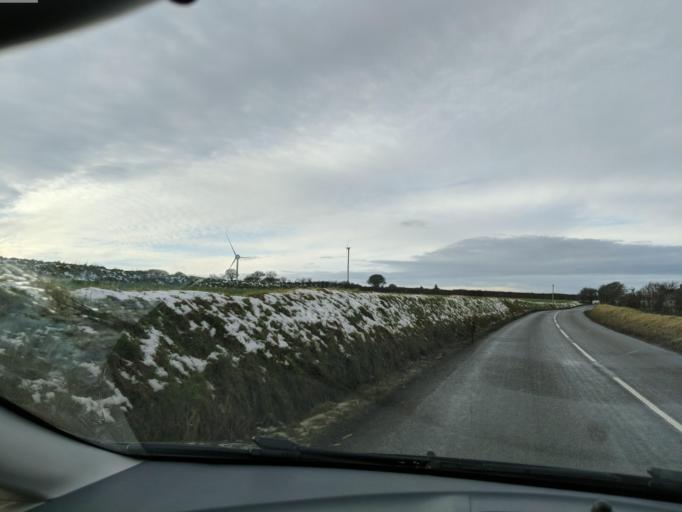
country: GB
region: England
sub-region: Cornwall
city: Jacobstow
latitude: 50.6642
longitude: -4.5897
